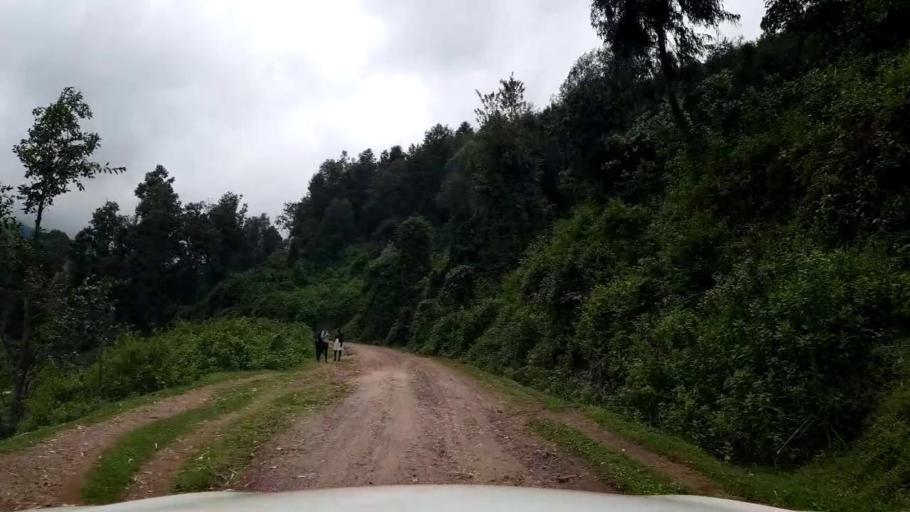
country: RW
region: Western Province
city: Gisenyi
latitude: -1.6496
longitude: 29.4145
